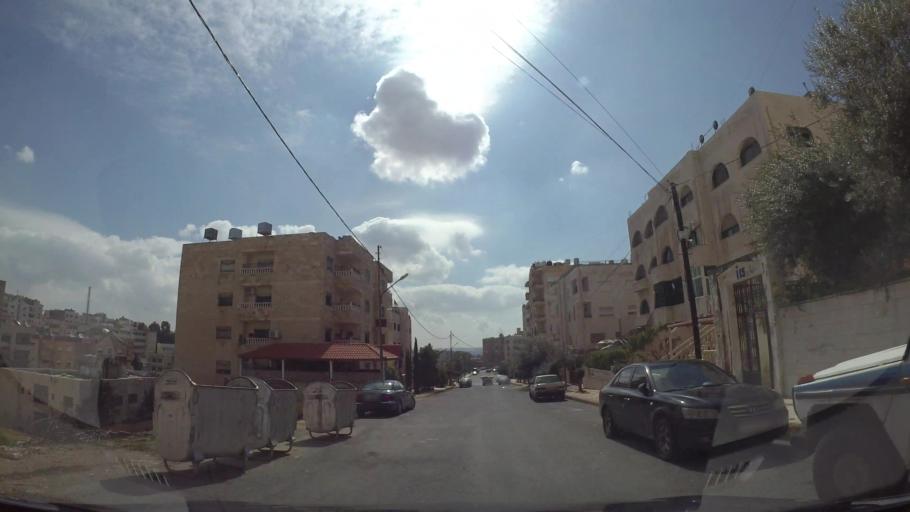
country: JO
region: Amman
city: Amman
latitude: 31.9923
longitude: 35.9069
